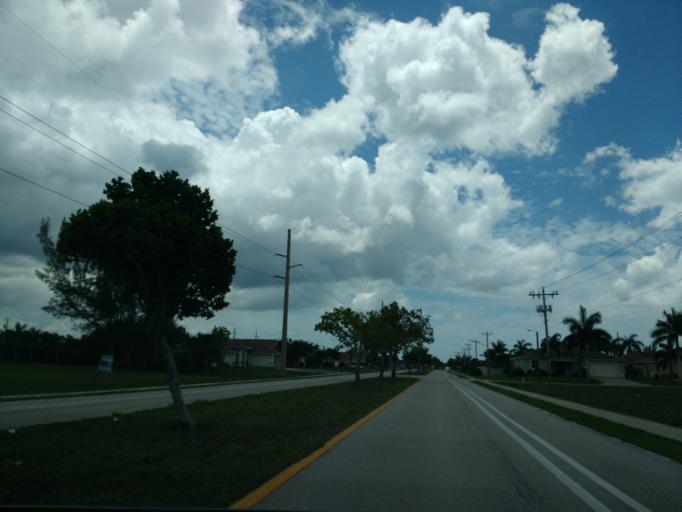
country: US
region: Florida
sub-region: Lee County
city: Cape Coral
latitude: 26.5657
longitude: -82.0173
